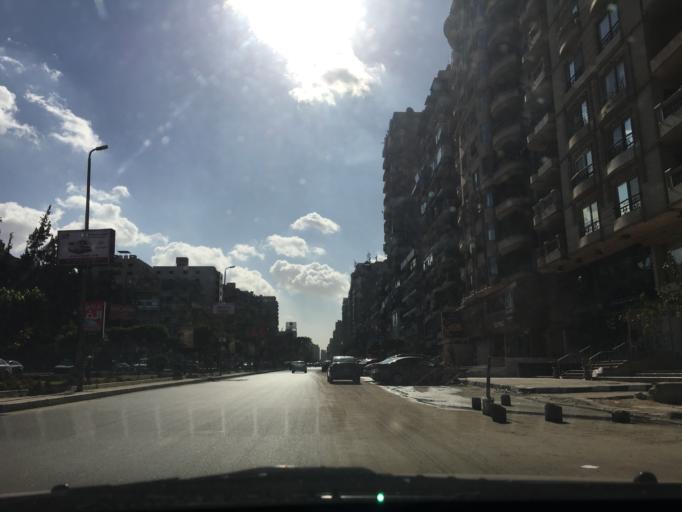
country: EG
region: Muhafazat al Qahirah
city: Cairo
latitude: 30.0617
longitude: 31.3450
